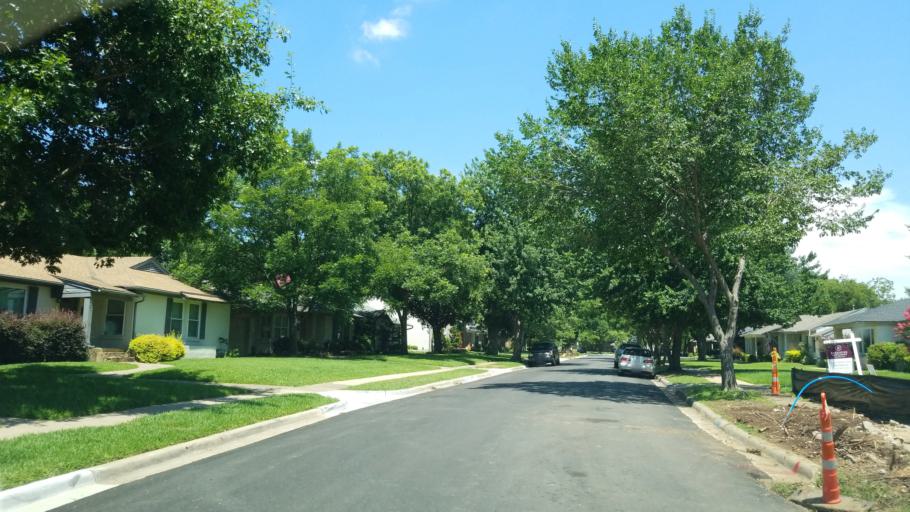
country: US
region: Texas
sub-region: Dallas County
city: University Park
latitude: 32.8735
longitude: -96.8427
